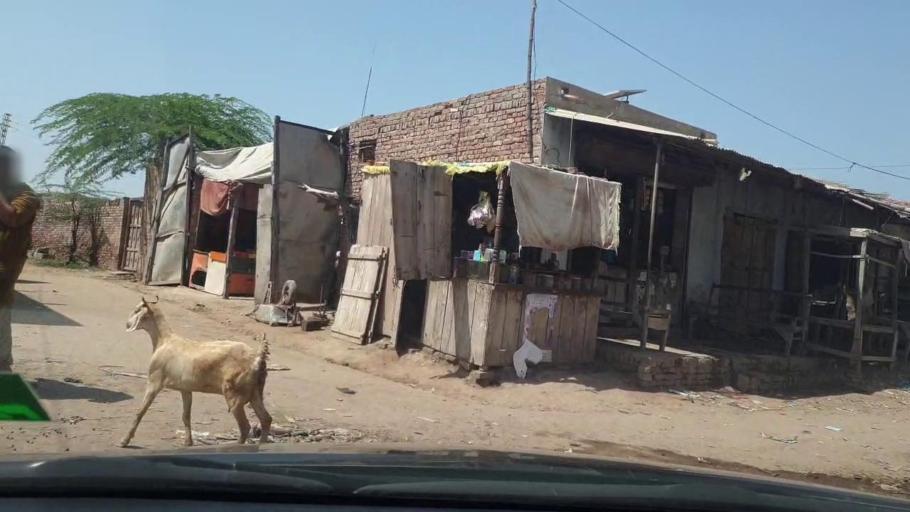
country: PK
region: Sindh
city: Tando Bago
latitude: 24.9251
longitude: 69.0573
